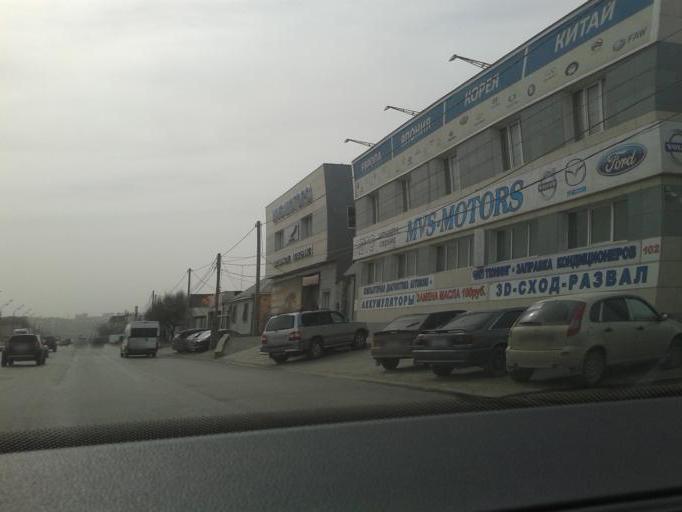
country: RU
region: Volgograd
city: Volgograd
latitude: 48.6941
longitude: 44.4651
